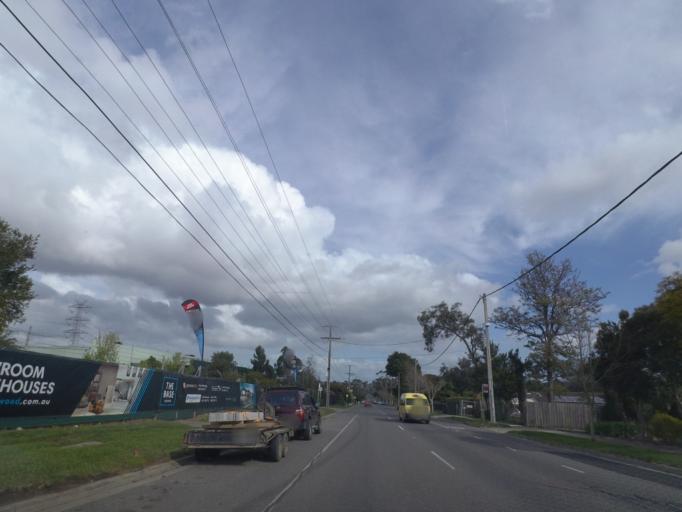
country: AU
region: Victoria
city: Mitcham
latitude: -37.8259
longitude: 145.2134
